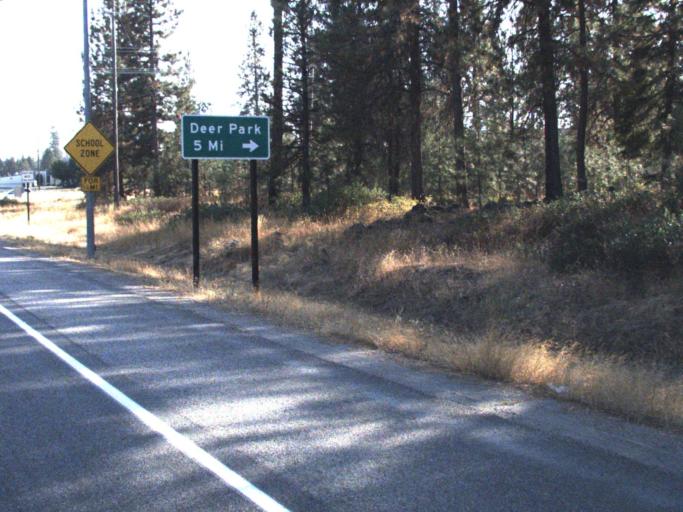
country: US
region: Washington
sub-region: Spokane County
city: Deer Park
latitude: 47.9718
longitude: -117.3496
